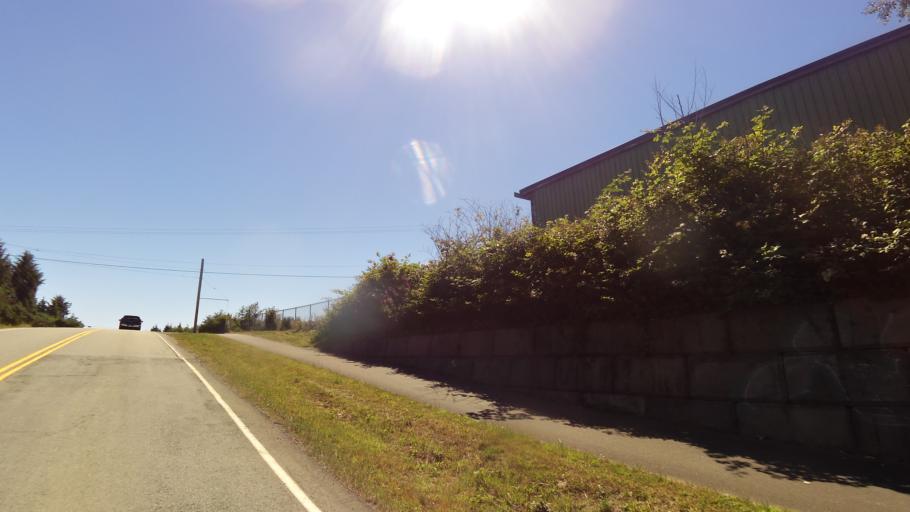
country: CA
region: British Columbia
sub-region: Regional District of Alberni-Clayoquot
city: Ucluelet
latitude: 48.9698
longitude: -125.5917
